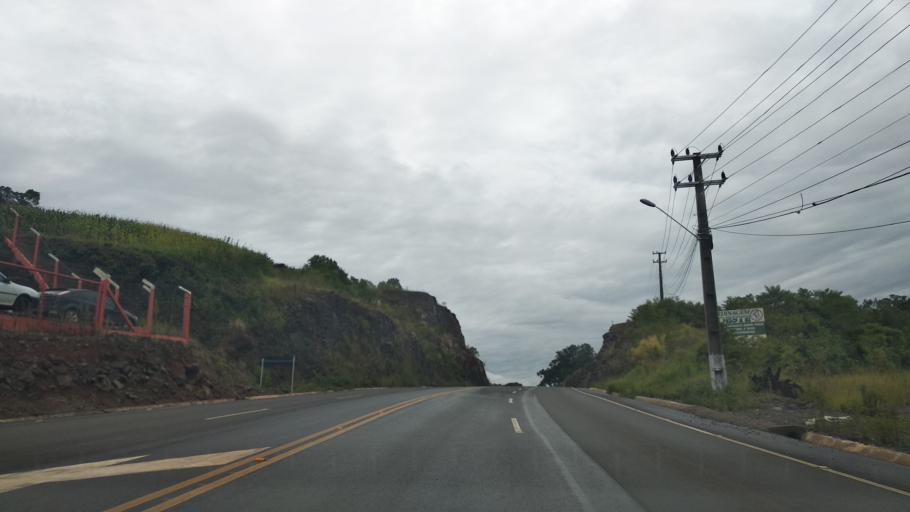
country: BR
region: Santa Catarina
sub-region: Videira
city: Videira
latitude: -27.0387
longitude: -51.1544
